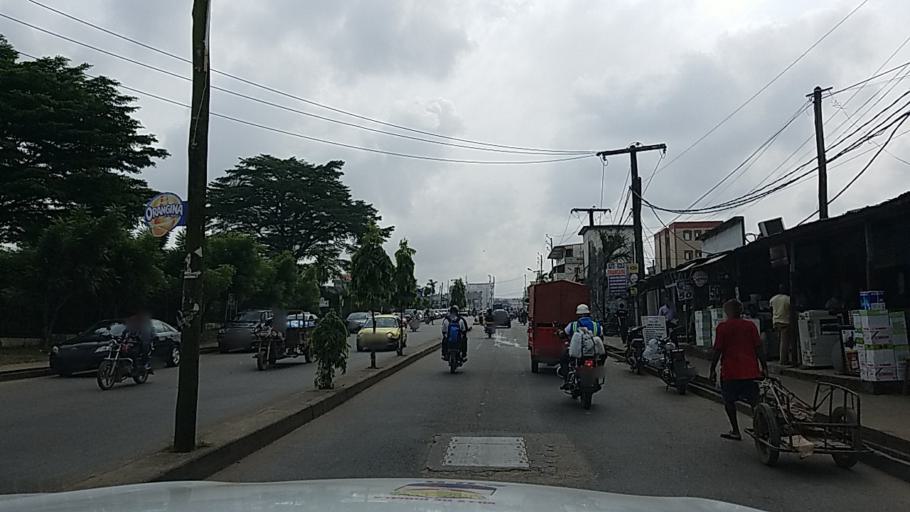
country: CM
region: Littoral
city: Douala
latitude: 4.0545
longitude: 9.7339
